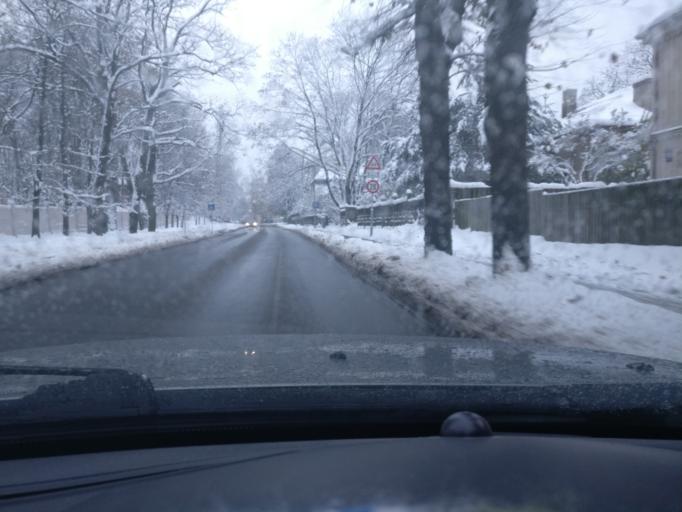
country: LV
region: Riga
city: Riga
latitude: 56.9308
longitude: 24.0817
